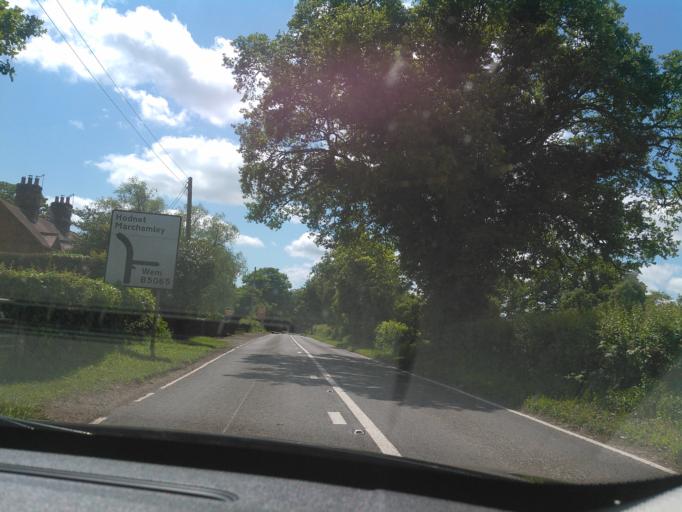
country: GB
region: England
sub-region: Shropshire
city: Prees
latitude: 52.8933
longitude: -2.6301
